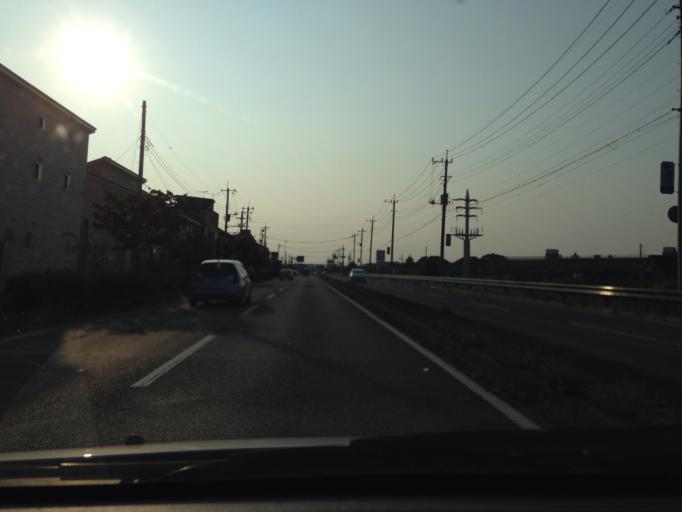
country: JP
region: Ibaraki
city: Ami
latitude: 36.0356
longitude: 140.2208
